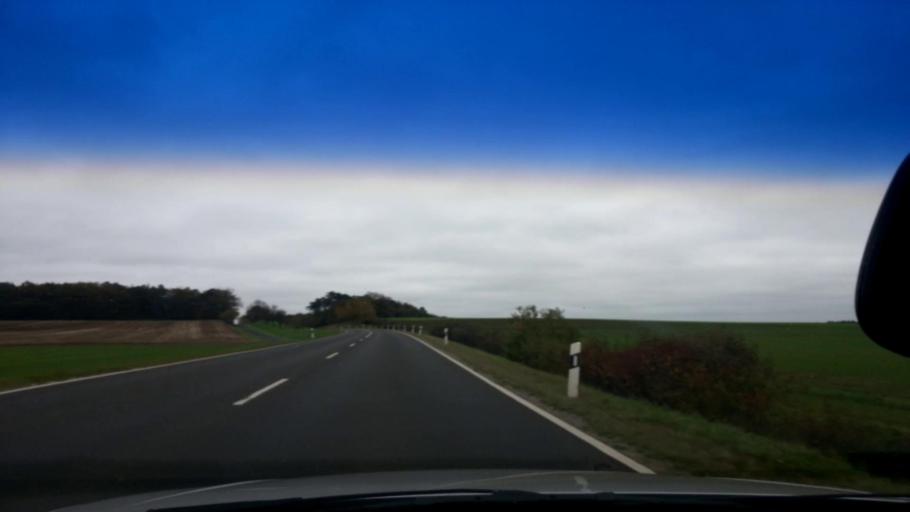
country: DE
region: Bavaria
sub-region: Upper Franconia
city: Walsdorf
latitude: 49.8330
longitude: 10.8060
